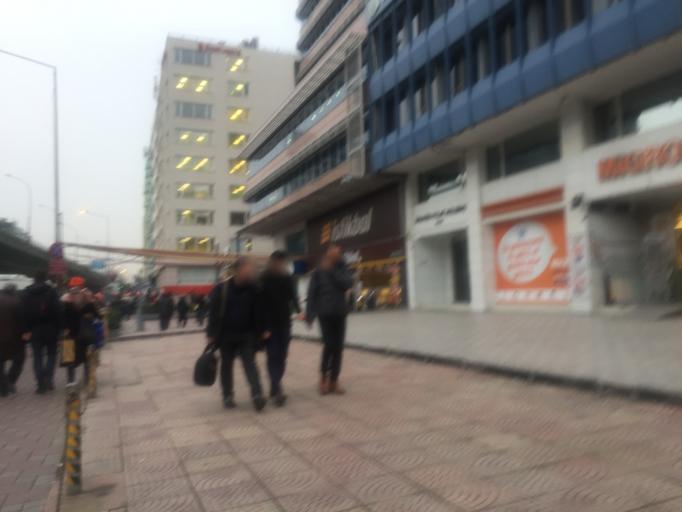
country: TR
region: Istanbul
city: Sisli
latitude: 41.0671
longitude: 29.0005
